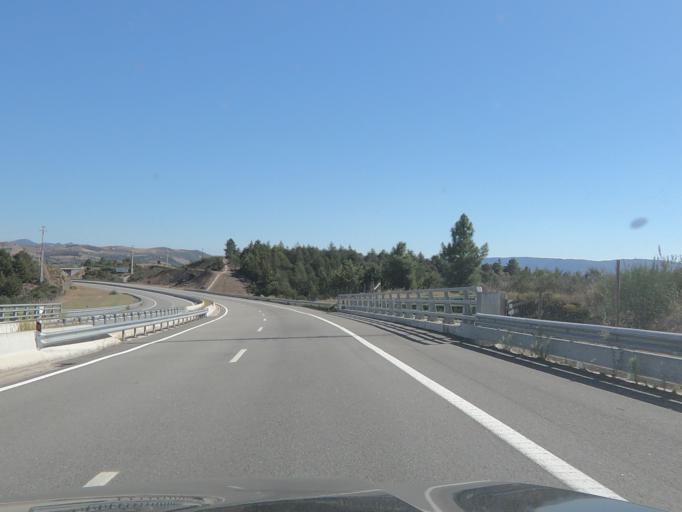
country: PT
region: Vila Real
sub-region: Murca
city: Murca
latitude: 41.4222
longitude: -7.3816
